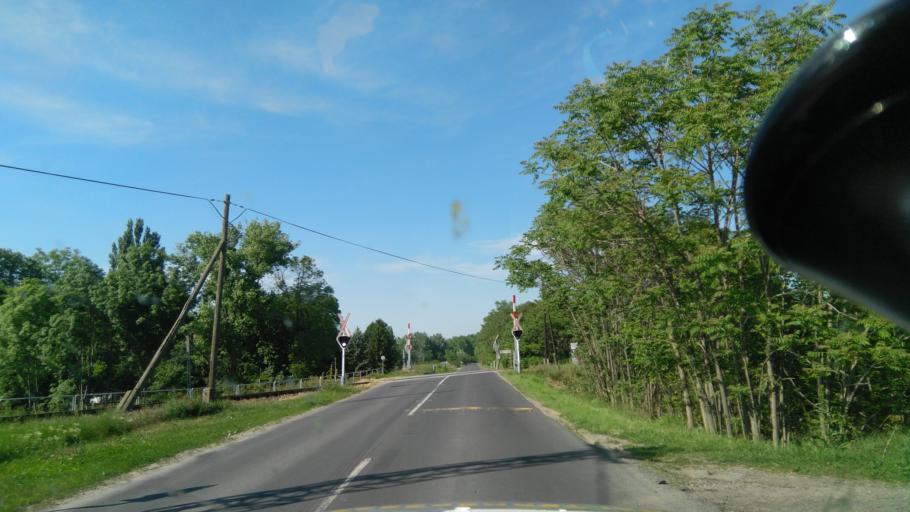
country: HU
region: Bekes
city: Gyula
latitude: 46.6729
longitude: 21.3008
